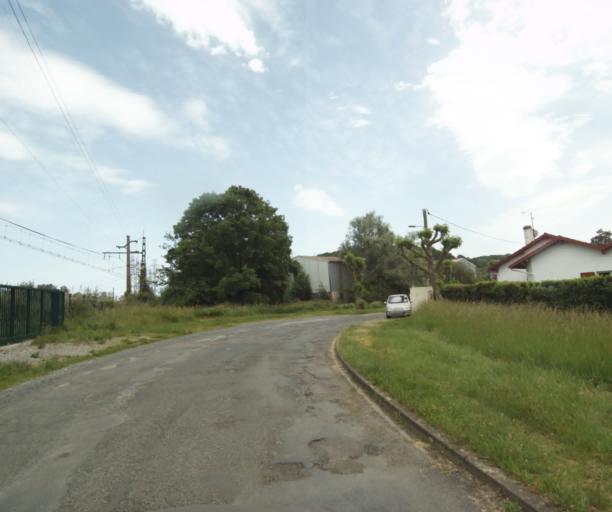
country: FR
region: Aquitaine
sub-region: Departement des Pyrenees-Atlantiques
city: Mouguerre
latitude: 43.4836
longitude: -1.4437
